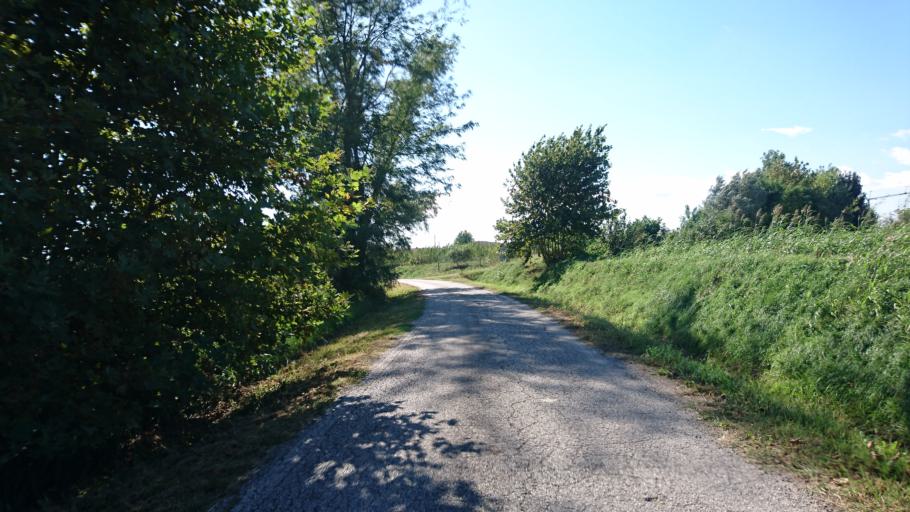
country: IT
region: Veneto
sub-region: Provincia di Venezia
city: Tombelle
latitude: 45.3996
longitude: 11.9880
